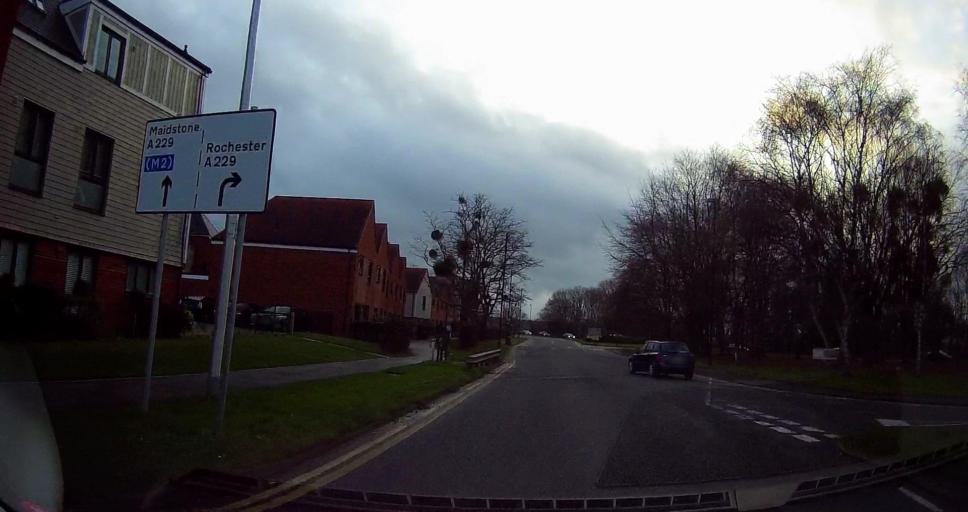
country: GB
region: England
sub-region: Kent
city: Chatham
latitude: 51.3582
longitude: 0.5104
